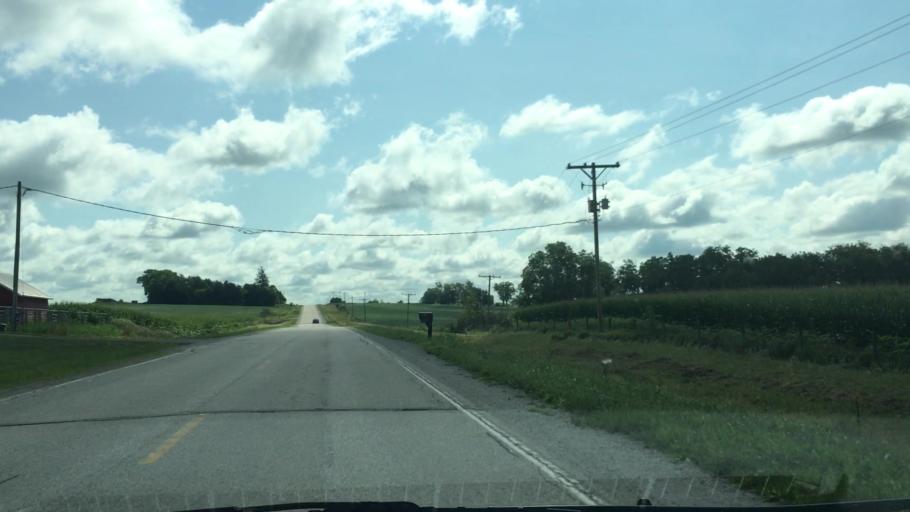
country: US
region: Iowa
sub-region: Johnson County
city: Solon
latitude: 41.8309
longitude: -91.4779
